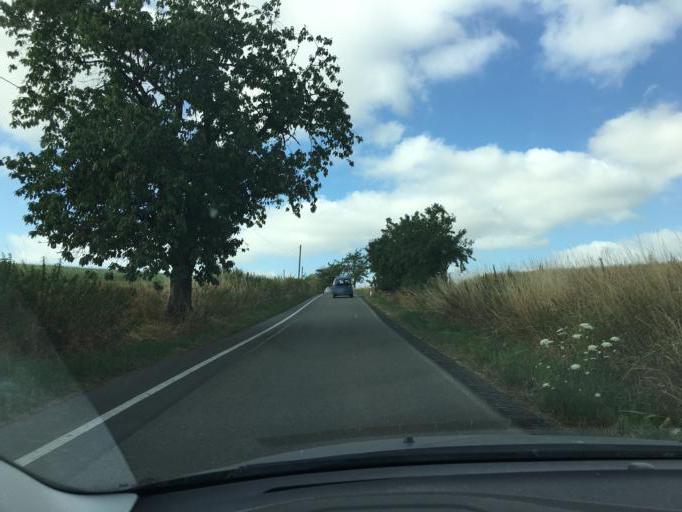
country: DE
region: Saxony
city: Frohburg
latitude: 51.0265
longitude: 12.6087
